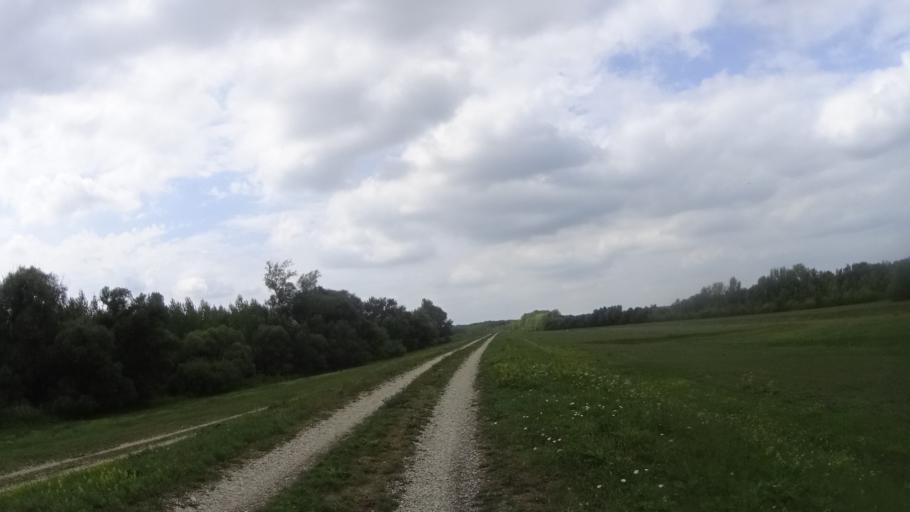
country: SK
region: Trnavsky
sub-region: Okres Dunajska Streda
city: Velky Meder
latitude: 47.7539
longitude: 17.7629
